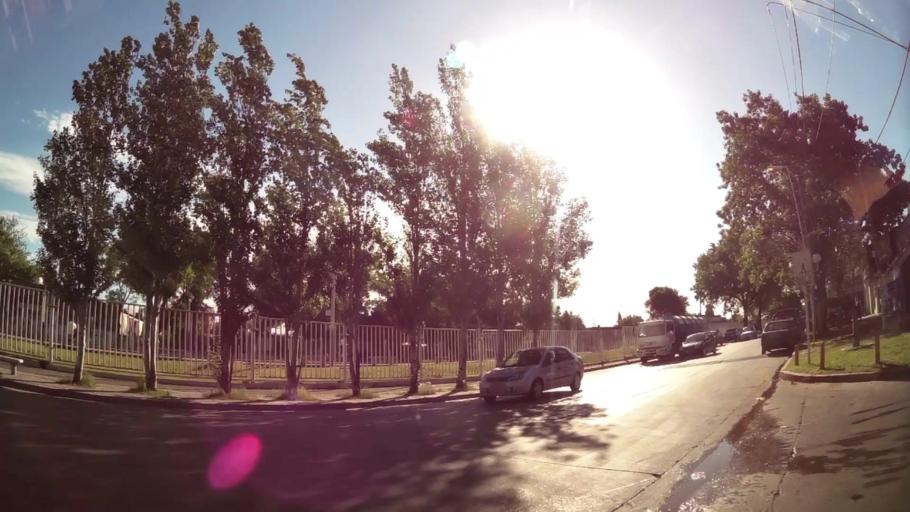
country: AR
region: Buenos Aires
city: Santa Catalina - Dique Lujan
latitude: -34.4939
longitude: -58.7056
